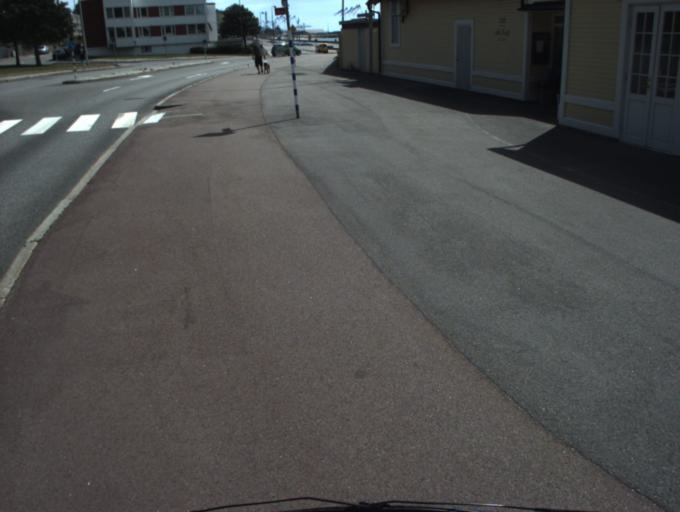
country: SE
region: Skane
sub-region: Helsingborg
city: Helsingborg
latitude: 56.0646
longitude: 12.6784
